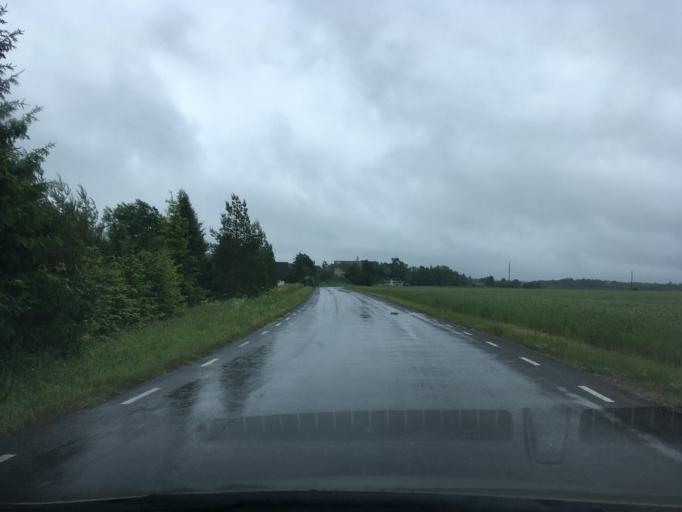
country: EE
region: Laeaene
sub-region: Lihula vald
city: Lihula
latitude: 58.6659
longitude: 23.7683
